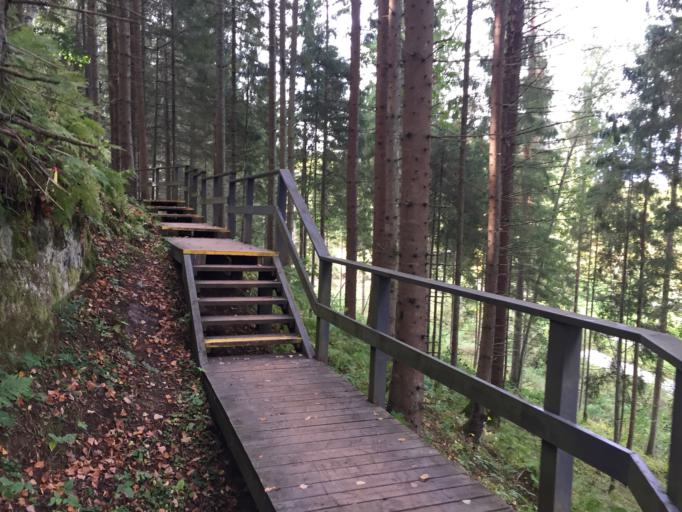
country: LV
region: Ligatne
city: Ligatne
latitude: 57.2308
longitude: 25.0447
